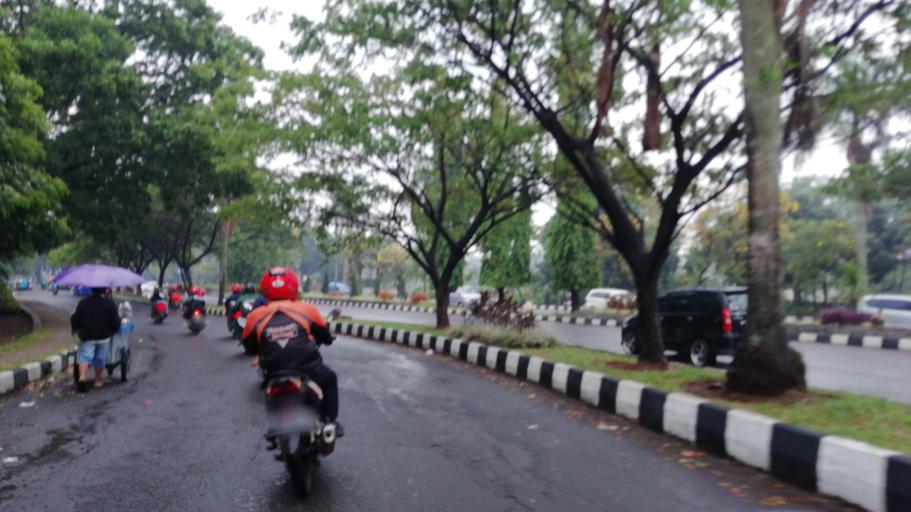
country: ID
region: West Java
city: Cibinong
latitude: -6.4827
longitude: 106.8197
